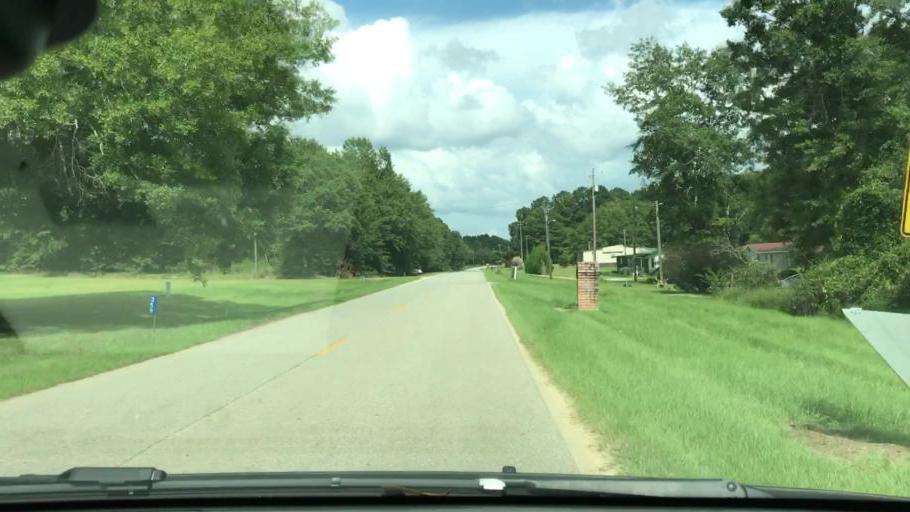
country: US
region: Georgia
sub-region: Clay County
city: Fort Gaines
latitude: 31.7181
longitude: -85.0600
